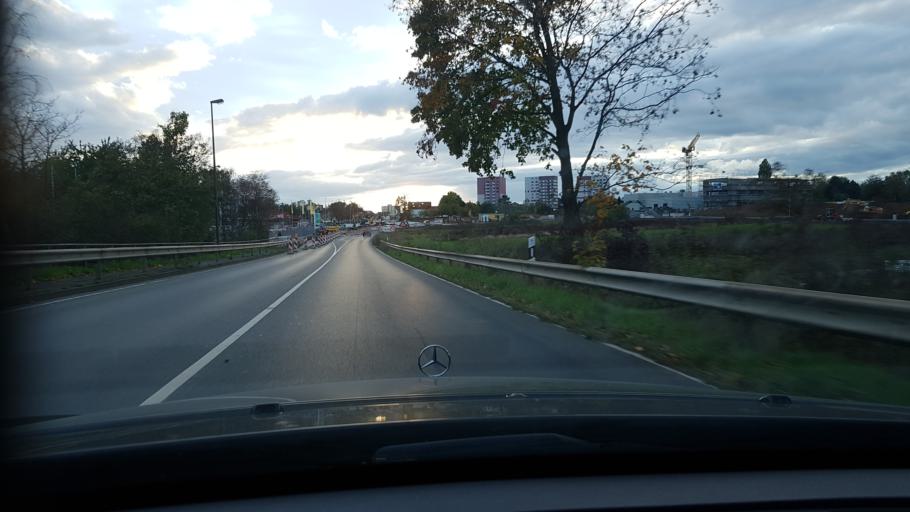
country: DE
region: Hesse
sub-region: Regierungsbezirk Darmstadt
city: Steinbach am Taunus
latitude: 50.1726
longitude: 8.5853
